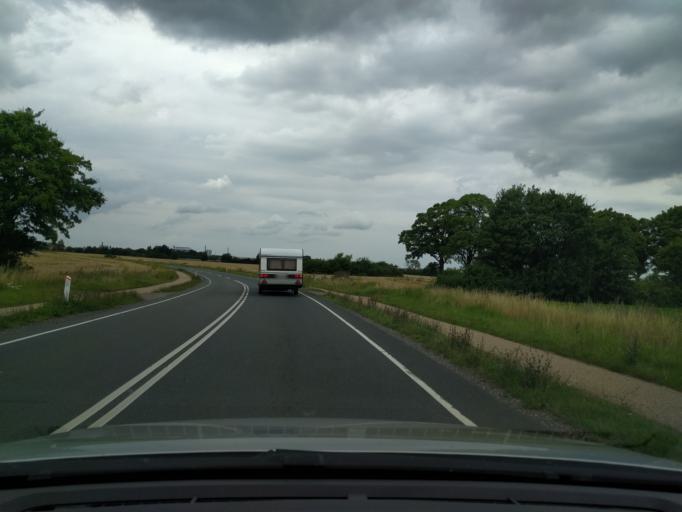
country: DK
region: Zealand
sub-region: Ringsted Kommune
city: Ringsted
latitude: 55.4242
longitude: 11.8227
